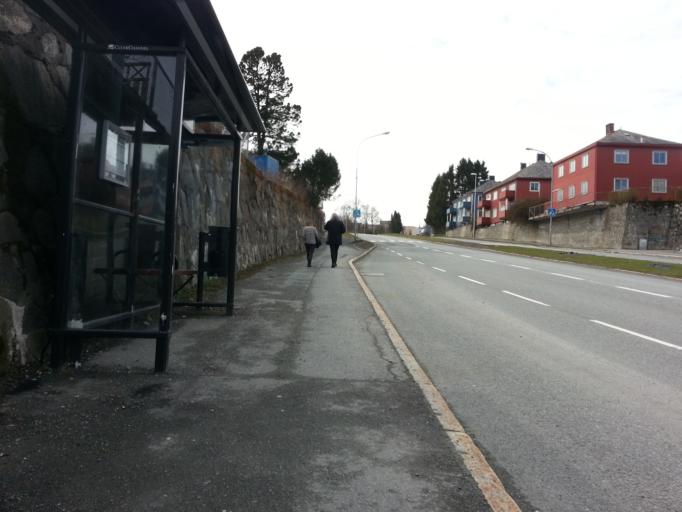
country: NO
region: Sor-Trondelag
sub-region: Trondheim
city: Trondheim
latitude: 63.4181
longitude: 10.3728
